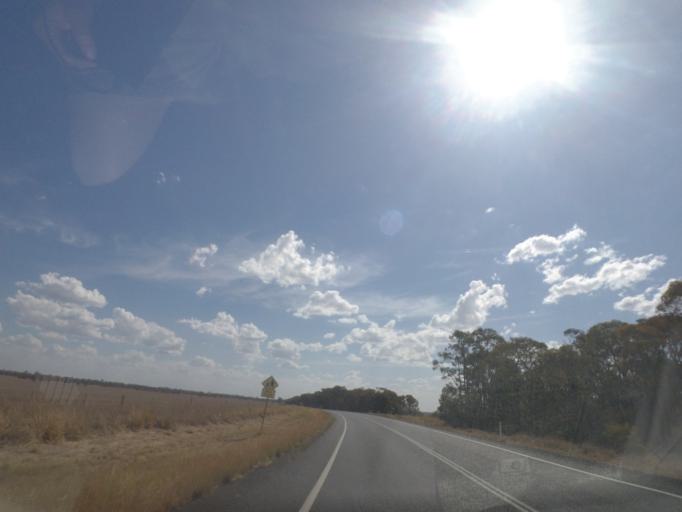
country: AU
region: Queensland
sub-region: Southern Downs
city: Stanthorpe
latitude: -28.4040
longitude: 151.1792
